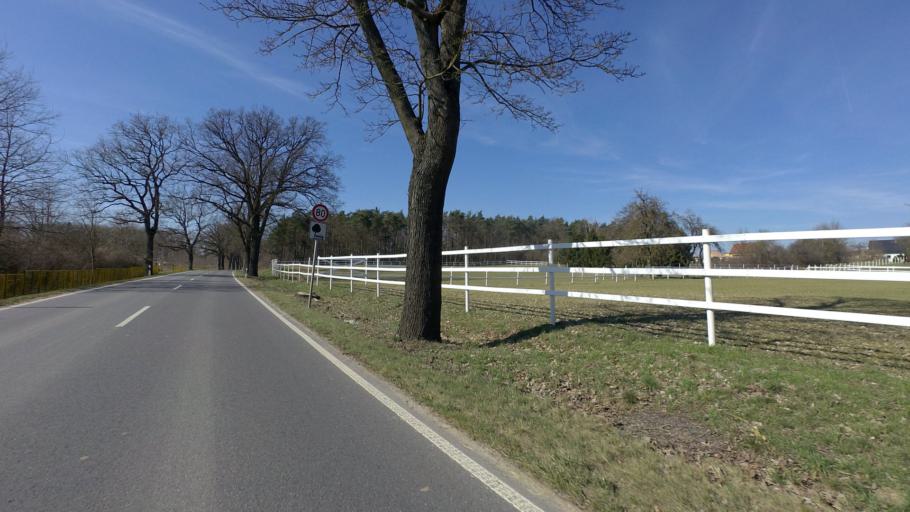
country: DE
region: Brandenburg
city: Waldsieversdorf
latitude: 52.5247
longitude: 14.0909
